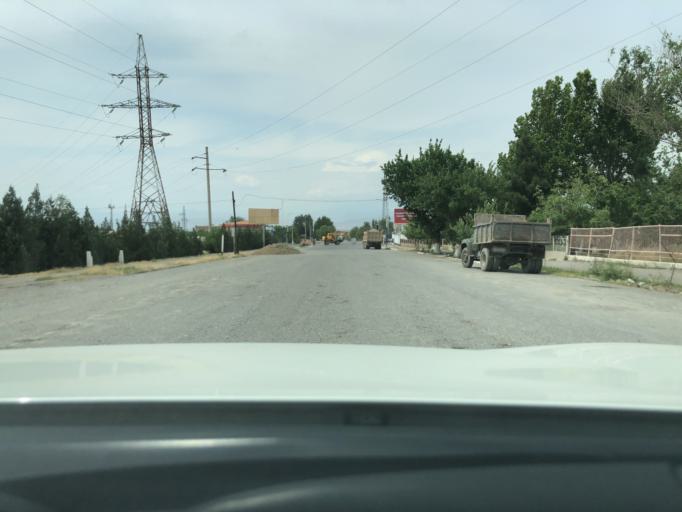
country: TJ
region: Viloyati Sughd
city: Konibodom
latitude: 40.2757
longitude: 70.4449
